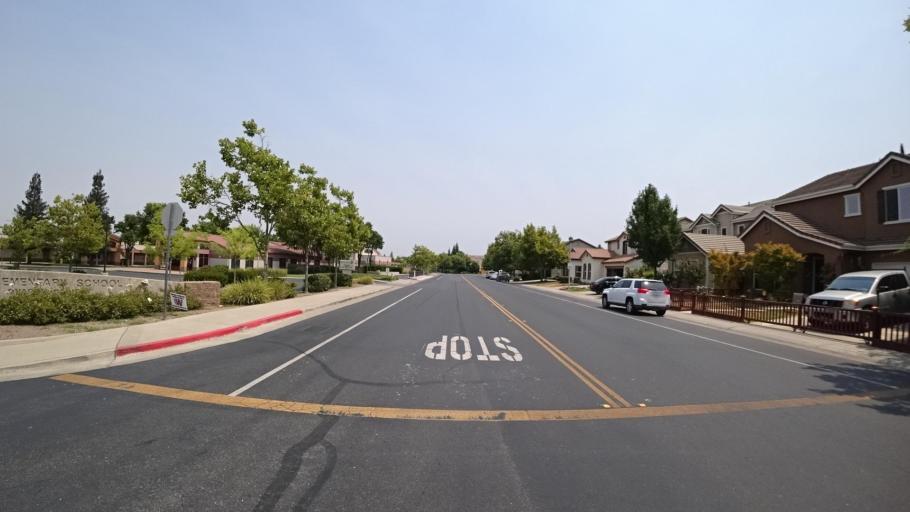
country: US
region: California
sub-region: Placer County
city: Rocklin
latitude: 38.7977
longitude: -121.2800
